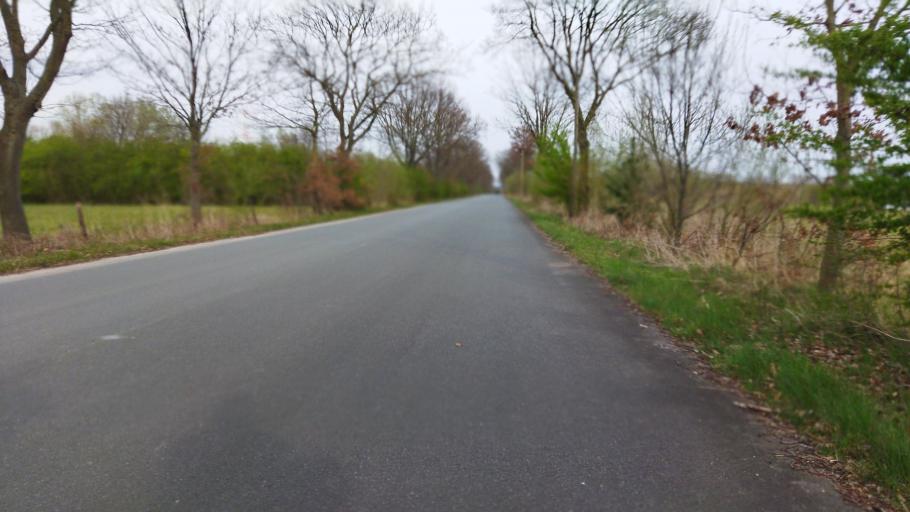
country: DE
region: Lower Saxony
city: Stolzenau
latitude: 52.5363
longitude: 9.0946
